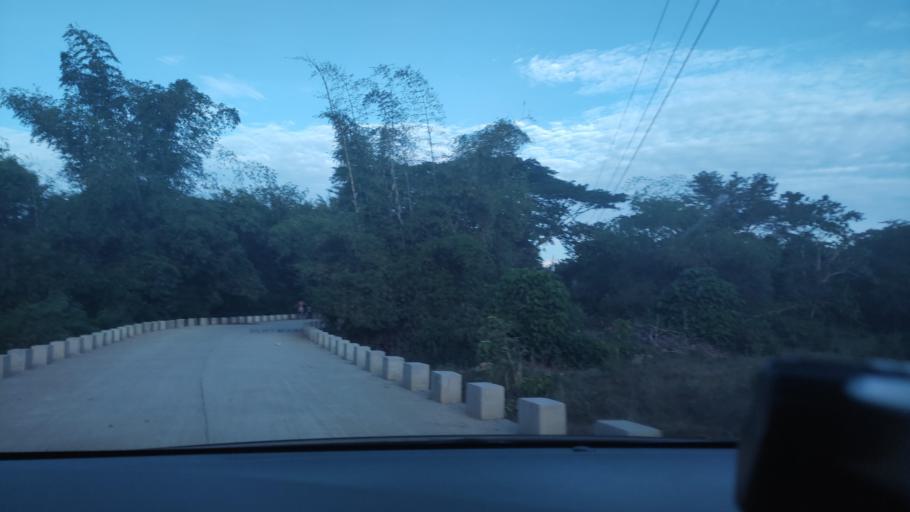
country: PH
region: Ilocos
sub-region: Province of Pangasinan
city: Balingasay
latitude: 16.3048
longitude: 119.8604
